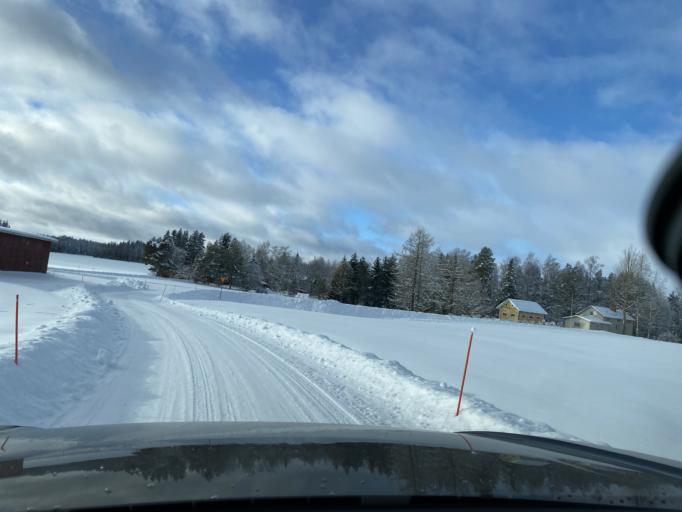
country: FI
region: Pirkanmaa
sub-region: Lounais-Pirkanmaa
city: Punkalaidun
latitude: 61.0742
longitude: 23.2217
